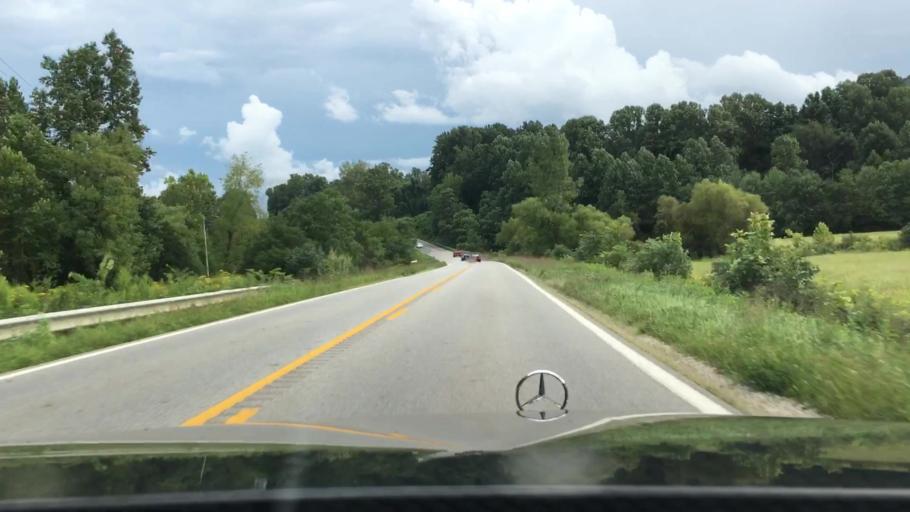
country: US
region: Virginia
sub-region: Nelson County
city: Nellysford
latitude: 37.9809
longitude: -78.8393
